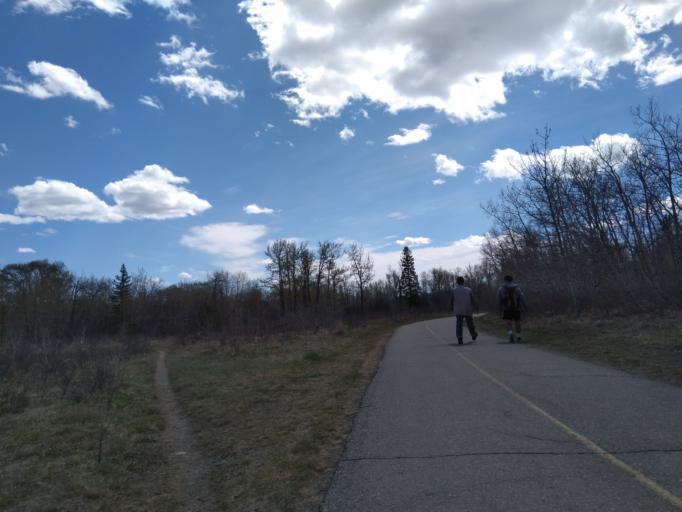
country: CA
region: Alberta
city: Calgary
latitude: 51.0915
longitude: -114.1811
